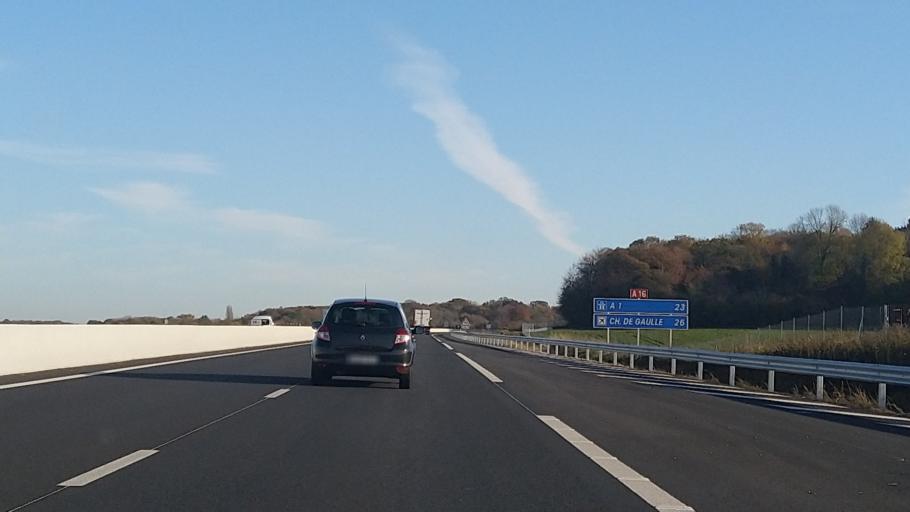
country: FR
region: Ile-de-France
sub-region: Departement du Val-d'Oise
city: Maffliers
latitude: 49.0985
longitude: 2.2879
